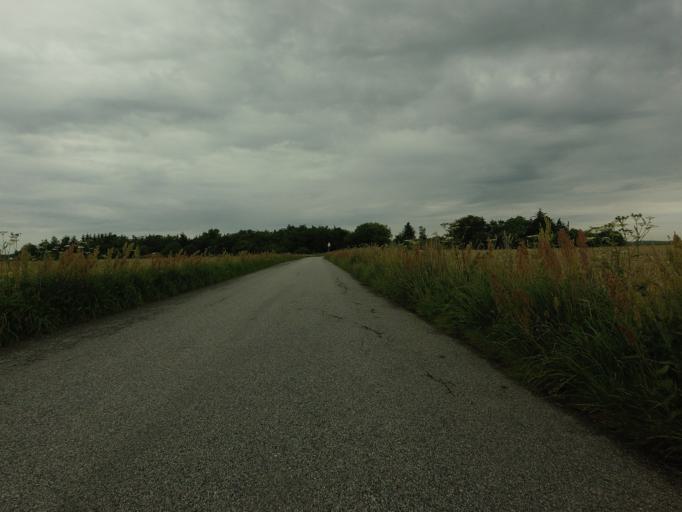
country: DK
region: North Denmark
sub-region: Alborg Kommune
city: Vadum
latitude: 57.1112
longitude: 9.8815
